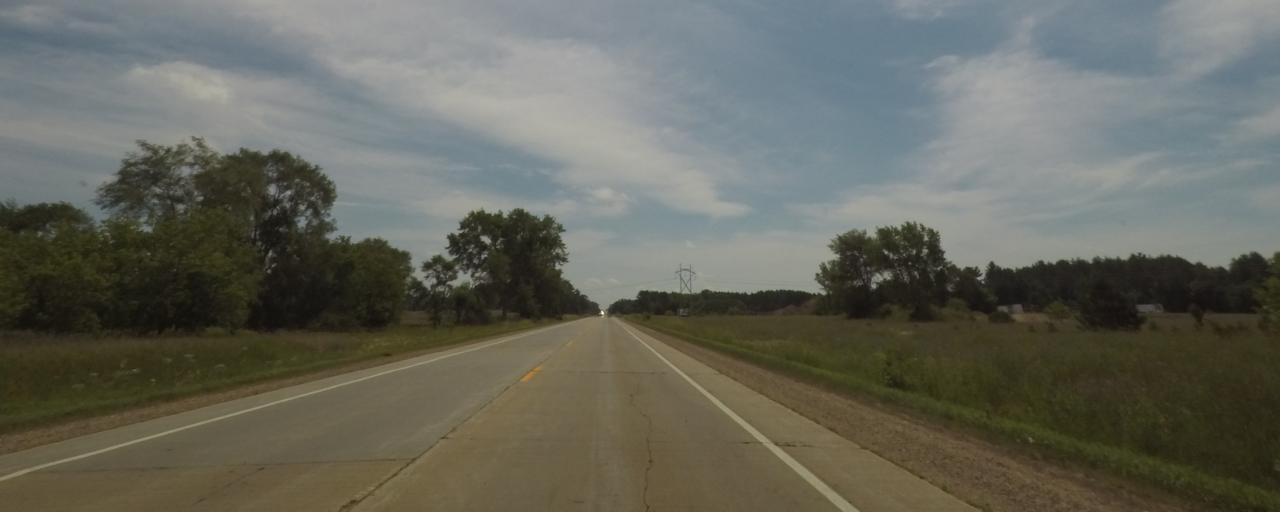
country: US
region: Wisconsin
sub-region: Portage County
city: Plover
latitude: 44.4421
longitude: -89.5352
